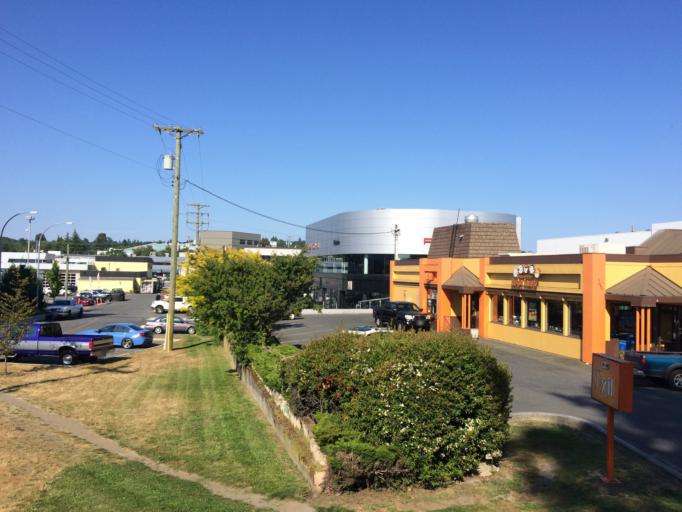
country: CA
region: British Columbia
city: Victoria
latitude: 48.4507
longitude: -123.3741
